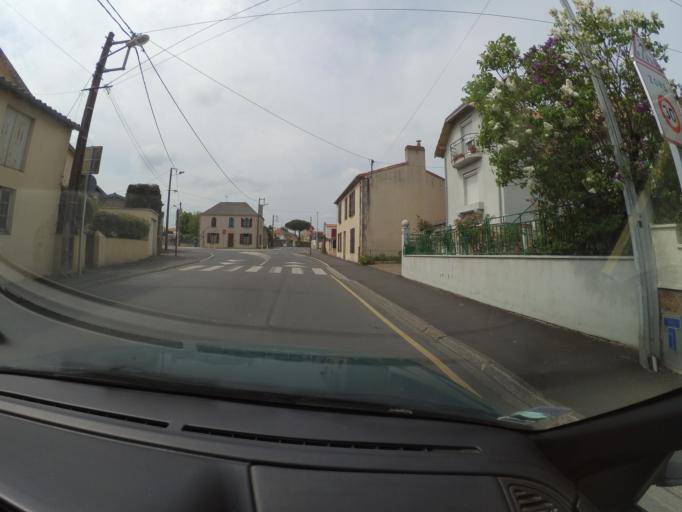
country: FR
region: Pays de la Loire
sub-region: Departement de la Loire-Atlantique
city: Clisson
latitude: 47.0904
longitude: -1.2875
